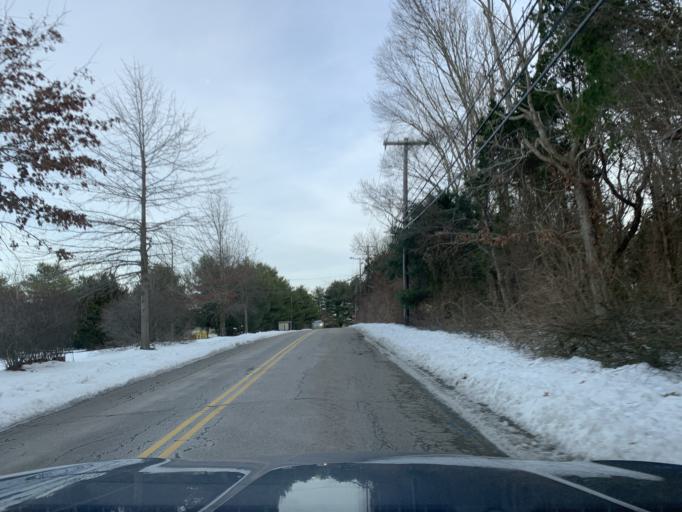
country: US
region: Rhode Island
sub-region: Washington County
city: North Kingstown
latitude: 41.5902
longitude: -71.4357
